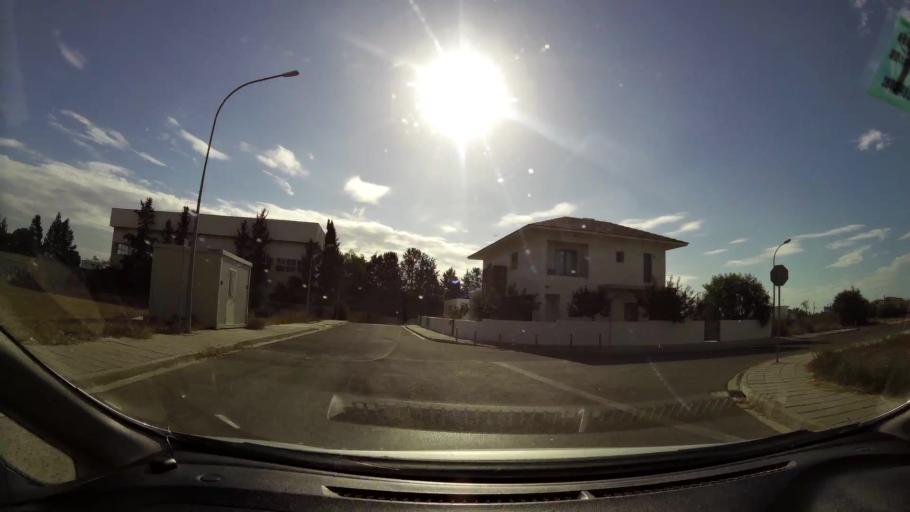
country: CY
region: Lefkosia
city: Nicosia
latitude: 35.1339
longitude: 33.3613
